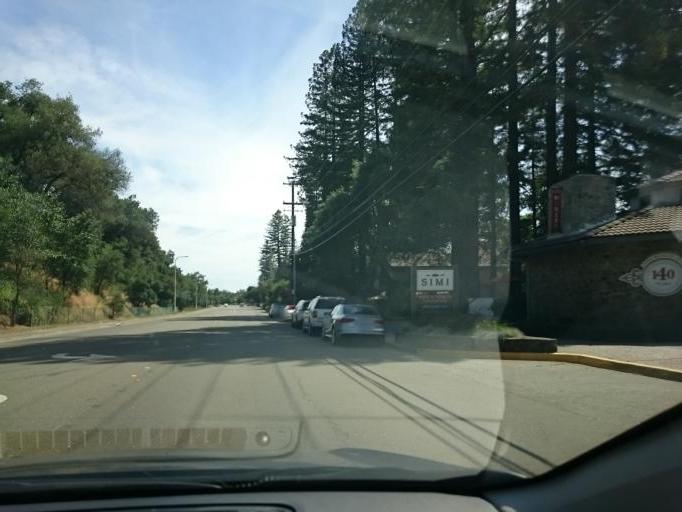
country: US
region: California
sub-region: Sonoma County
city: Healdsburg
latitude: 38.6406
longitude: -122.8734
